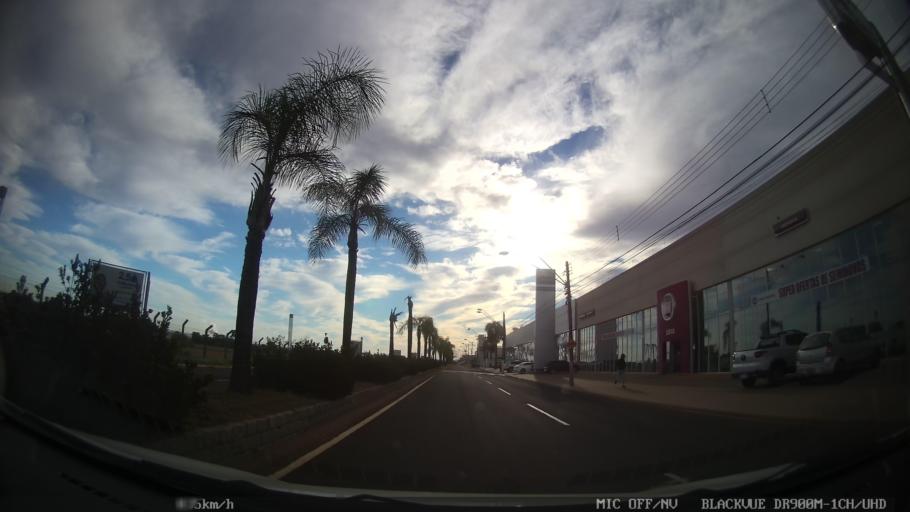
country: BR
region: Sao Paulo
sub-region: Catanduva
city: Catanduva
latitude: -21.1515
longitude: -48.9902
